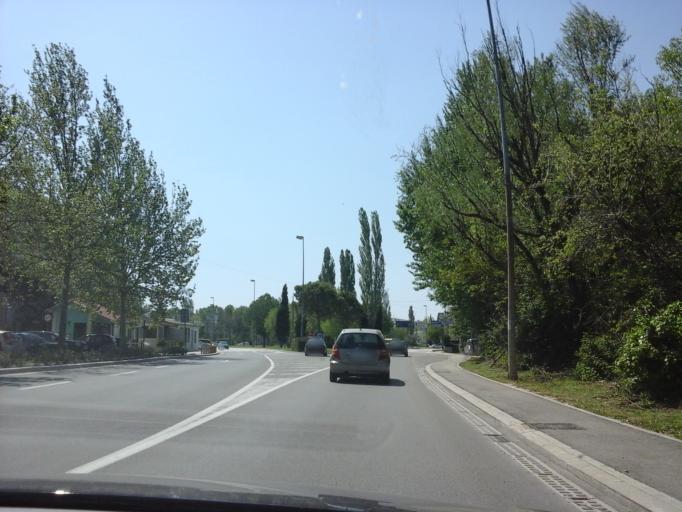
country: HR
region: Splitsko-Dalmatinska
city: Solin
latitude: 43.5365
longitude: 16.4868
